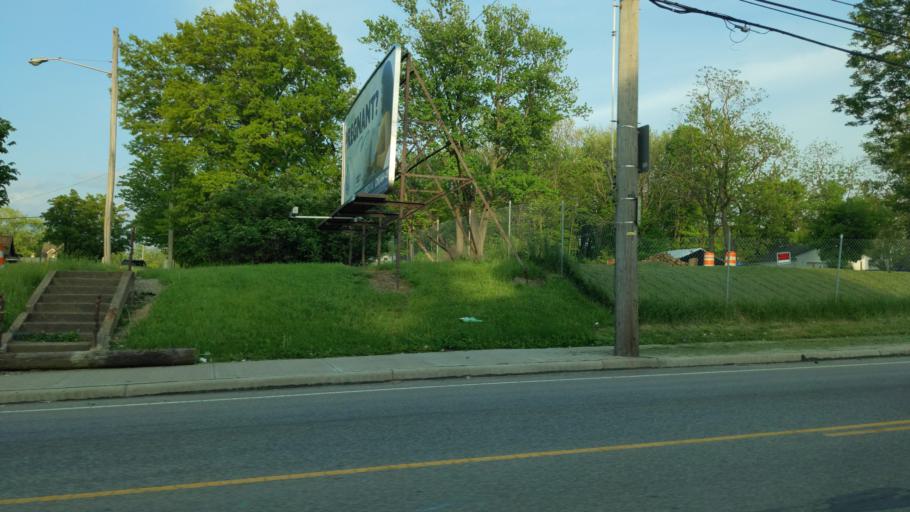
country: US
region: Ohio
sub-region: Cuyahoga County
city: Brook Park
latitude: 41.4327
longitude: -81.7800
